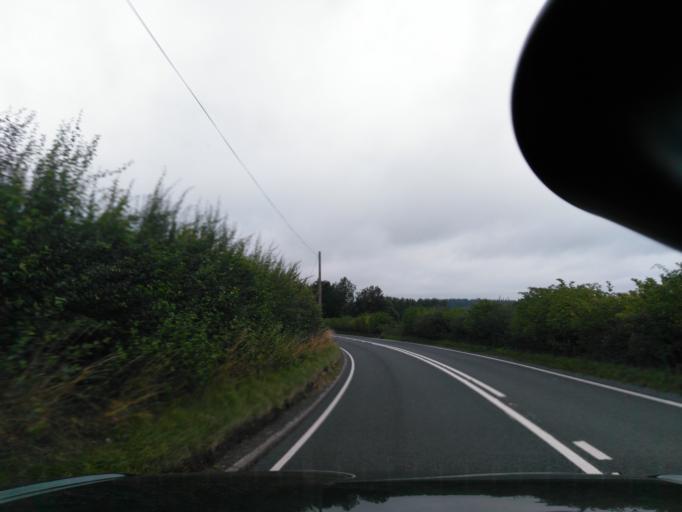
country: GB
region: England
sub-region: Wiltshire
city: Bishopstrow
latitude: 51.1617
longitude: -2.1805
